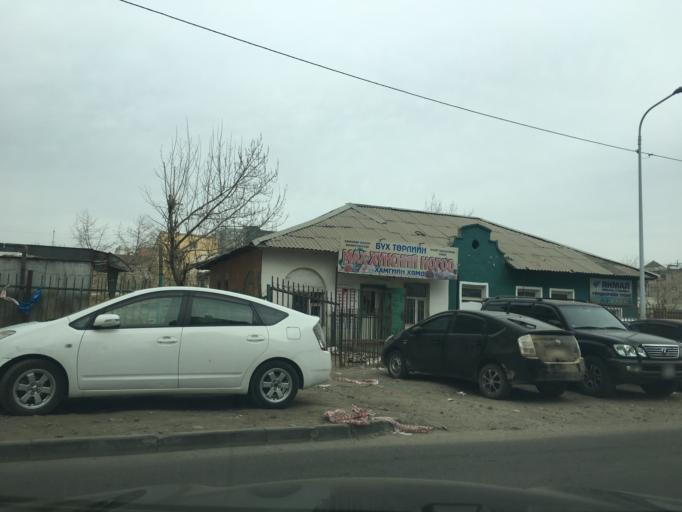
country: MN
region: Ulaanbaatar
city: Ulaanbaatar
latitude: 47.9107
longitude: 106.8893
